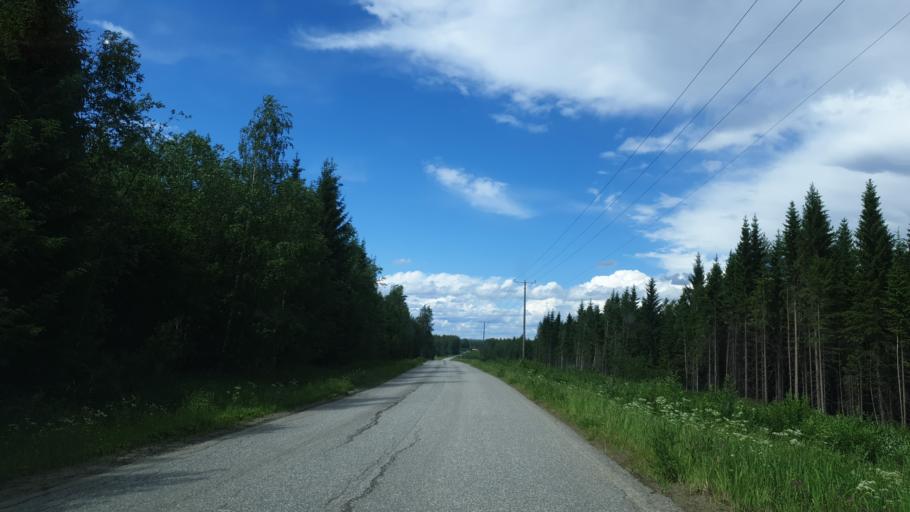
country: FI
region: Northern Savo
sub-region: Koillis-Savo
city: Kaavi
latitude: 62.9808
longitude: 28.7443
